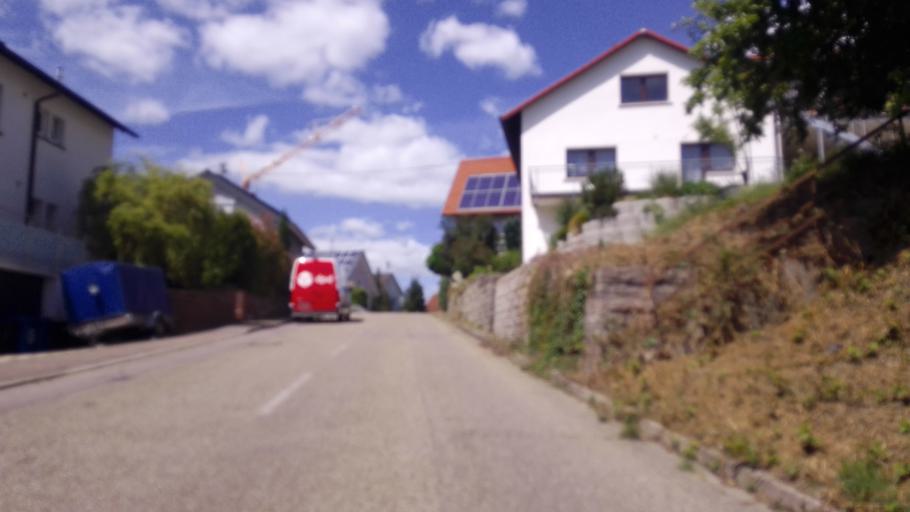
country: DE
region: Baden-Wuerttemberg
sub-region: Karlsruhe Region
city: Sinzheim
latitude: 48.7287
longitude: 8.1766
